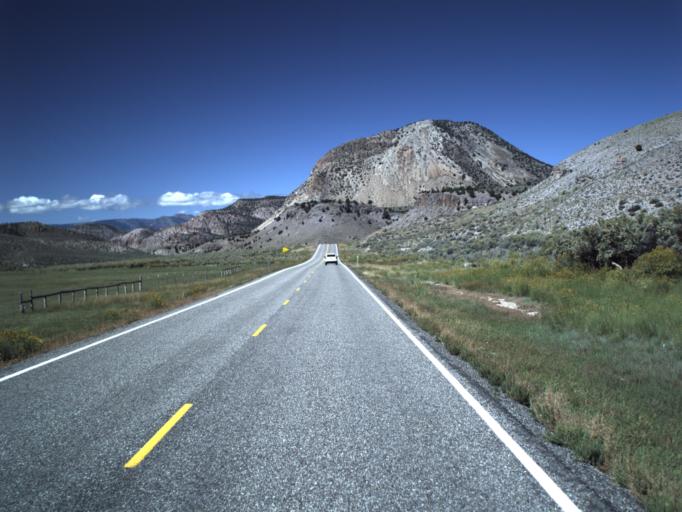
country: US
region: Utah
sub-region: Piute County
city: Junction
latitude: 38.1706
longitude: -112.0584
